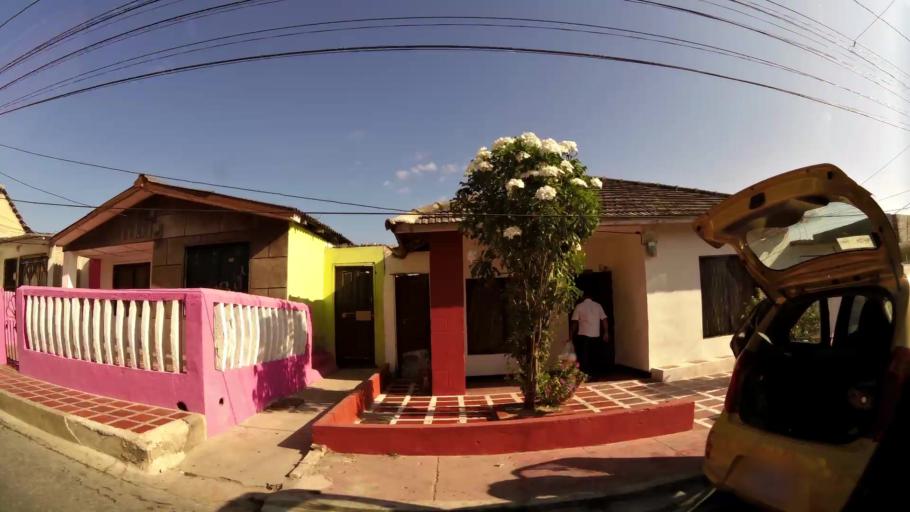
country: CO
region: Atlantico
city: Barranquilla
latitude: 10.9903
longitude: -74.7850
